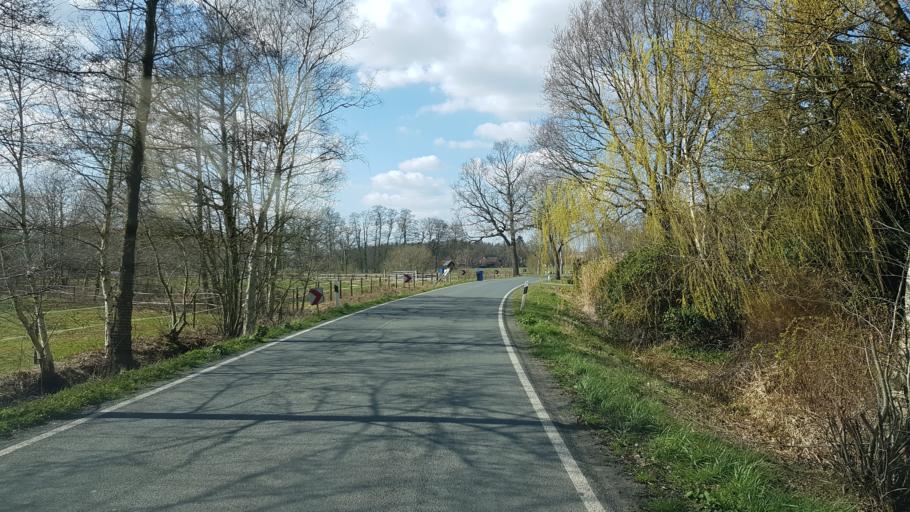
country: DE
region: Lower Saxony
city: Rastede
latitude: 53.3107
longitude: 8.2377
